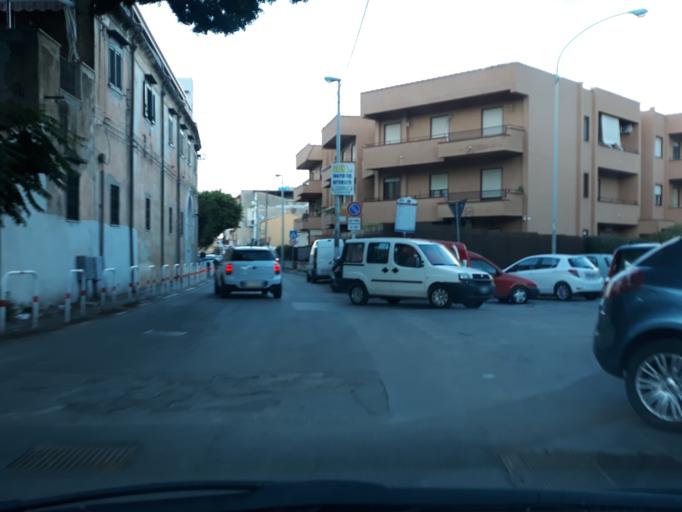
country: IT
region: Sicily
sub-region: Palermo
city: Villa Ciambra
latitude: 38.0926
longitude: 13.3342
